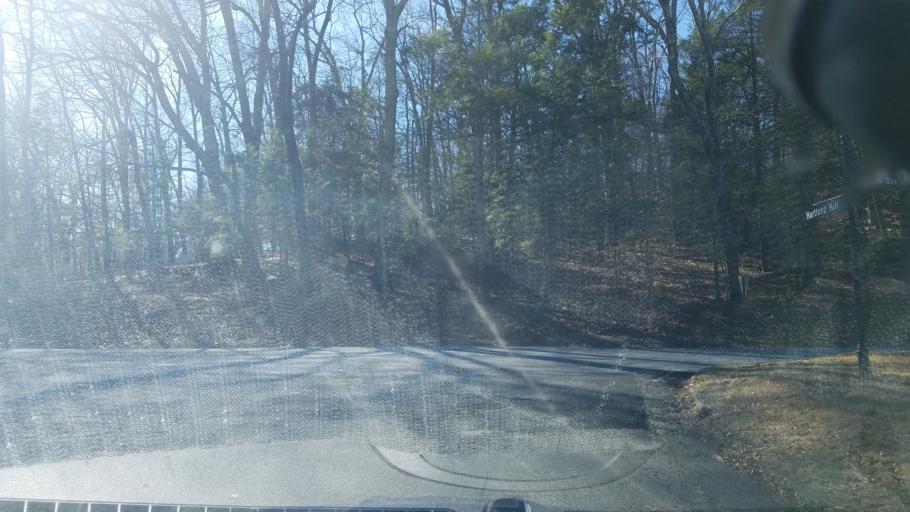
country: US
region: Connecticut
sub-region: New Haven County
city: Heritage Village
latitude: 41.4972
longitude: -73.2676
